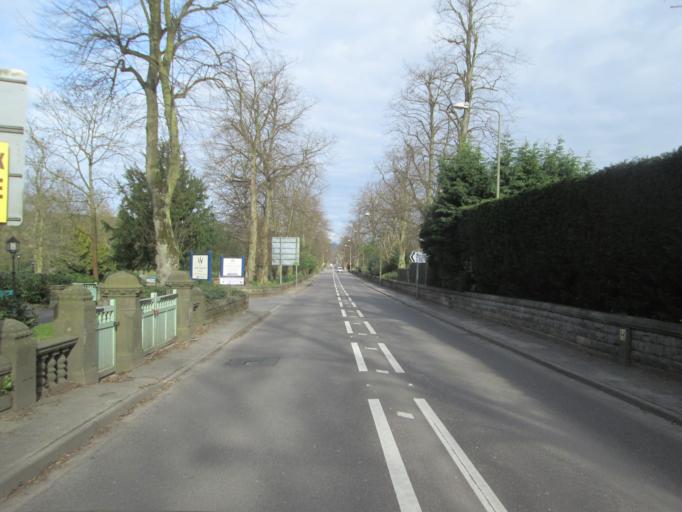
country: GB
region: England
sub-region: Derbyshire
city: Matlock
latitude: 53.1627
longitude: -1.5903
